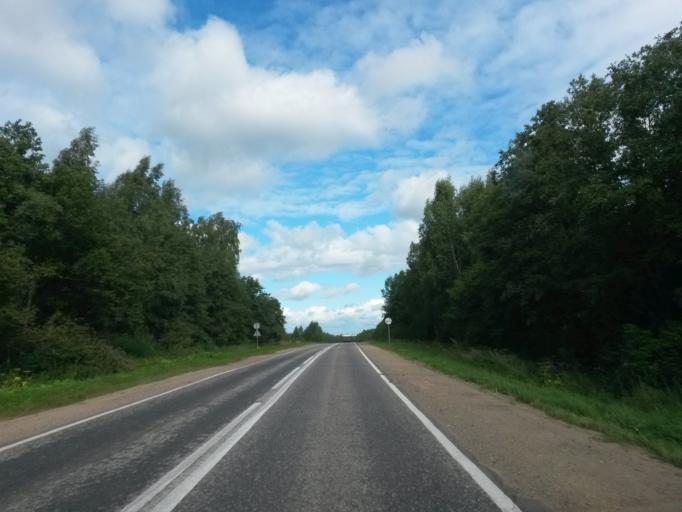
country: RU
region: Jaroslavl
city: Krasnyye Tkachi
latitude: 57.4814
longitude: 39.9048
